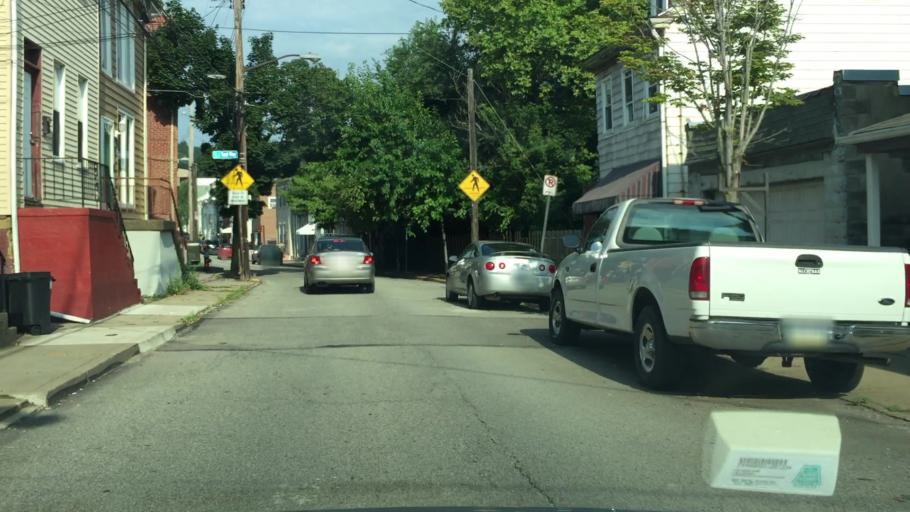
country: US
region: Pennsylvania
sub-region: Allegheny County
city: Mount Oliver
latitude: 40.4243
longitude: -79.9798
